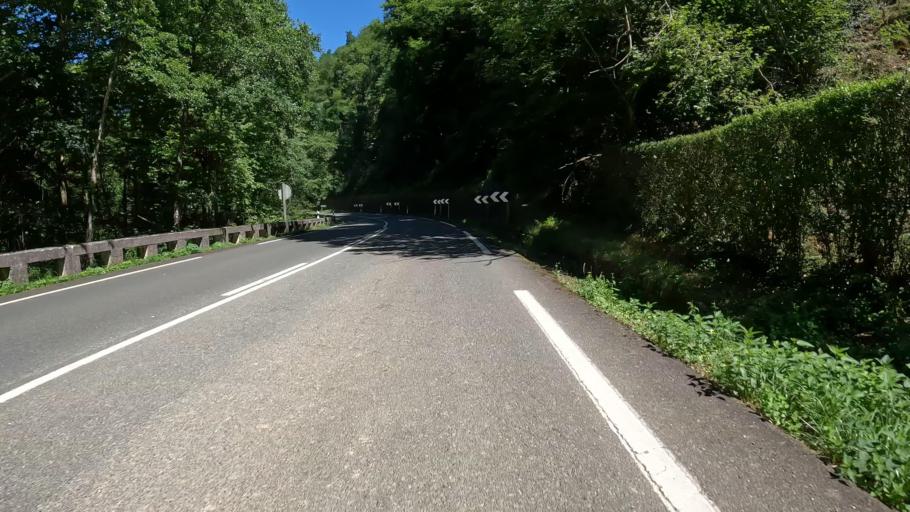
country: ES
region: Basque Country
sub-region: Provincia de Guipuzcoa
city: Oreja
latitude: 43.0734
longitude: -2.0117
